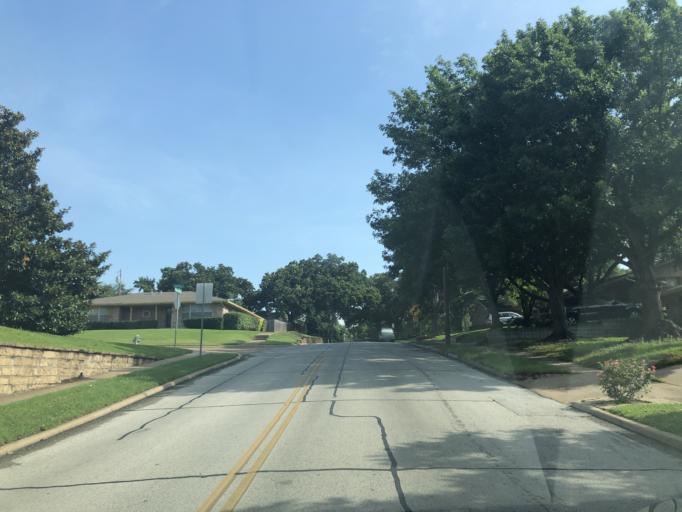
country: US
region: Texas
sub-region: Dallas County
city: Irving
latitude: 32.7996
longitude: -96.9689
